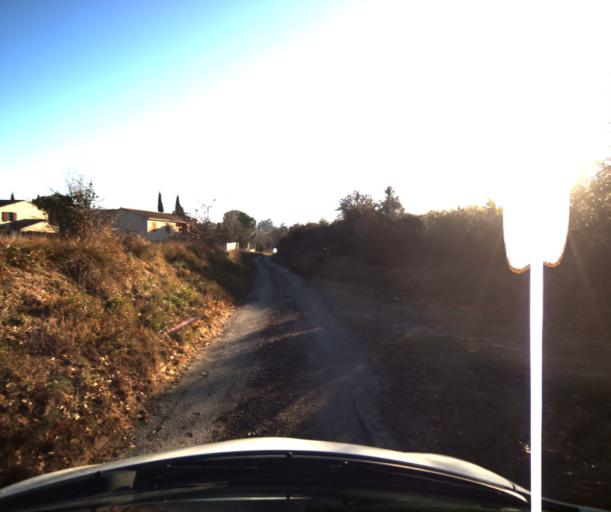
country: FR
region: Provence-Alpes-Cote d'Azur
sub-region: Departement du Vaucluse
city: Pertuis
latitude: 43.7054
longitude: 5.4928
